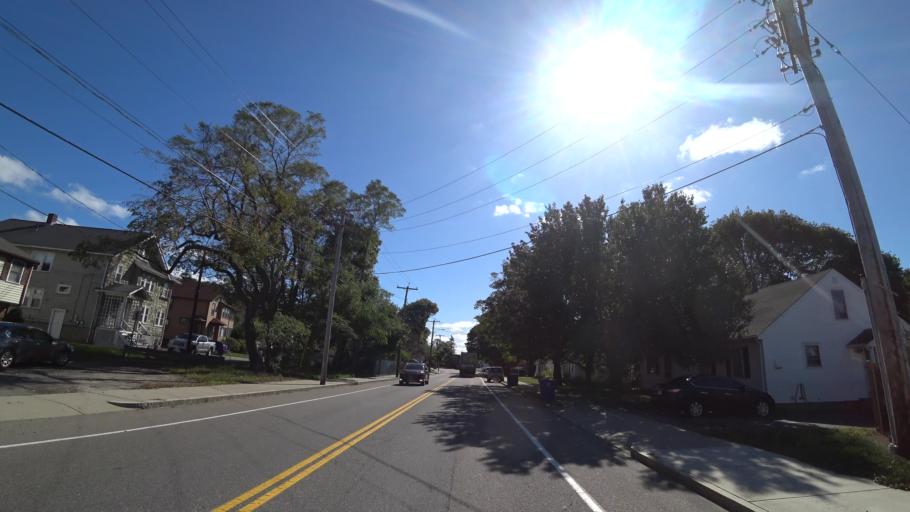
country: US
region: Massachusetts
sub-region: Norfolk County
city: Braintree
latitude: 42.2254
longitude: -71.0031
